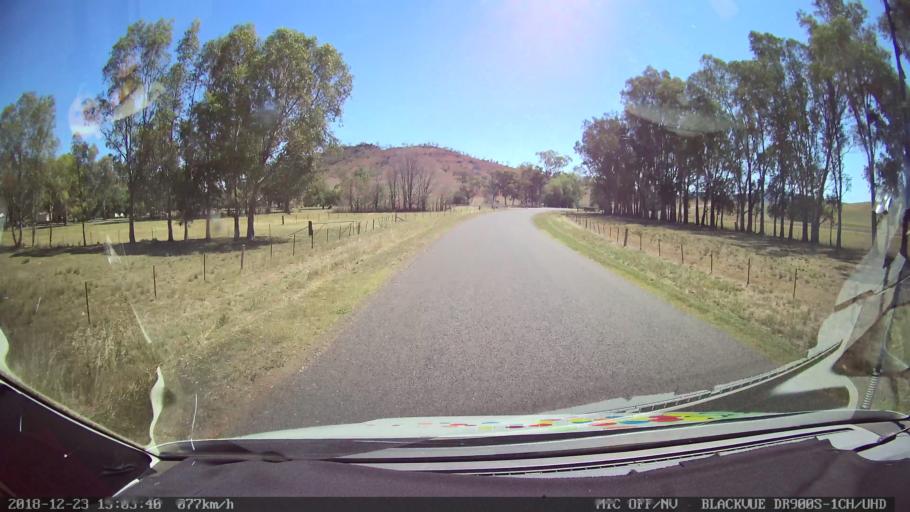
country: AU
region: New South Wales
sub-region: Tamworth Municipality
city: Manilla
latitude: -30.7403
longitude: 150.7627
